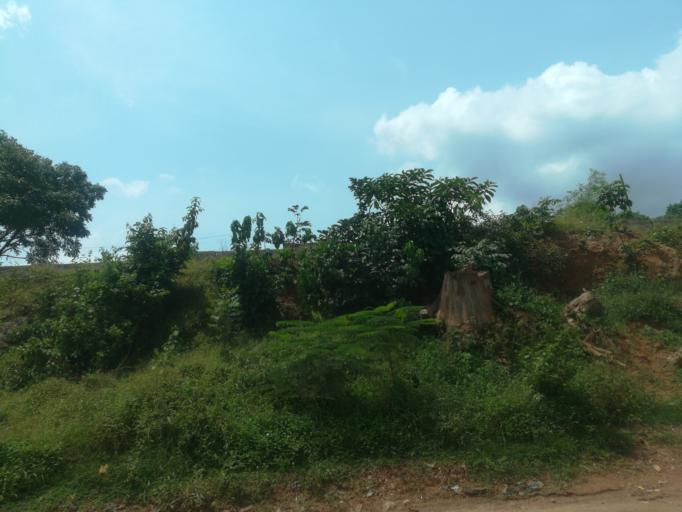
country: NG
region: Oyo
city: Ibadan
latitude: 7.4494
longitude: 3.9508
